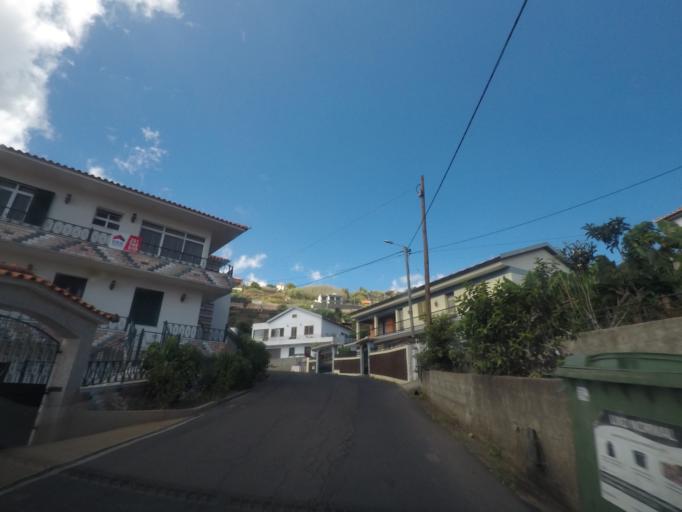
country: PT
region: Madeira
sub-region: Ribeira Brava
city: Campanario
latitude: 32.6724
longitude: -17.0481
